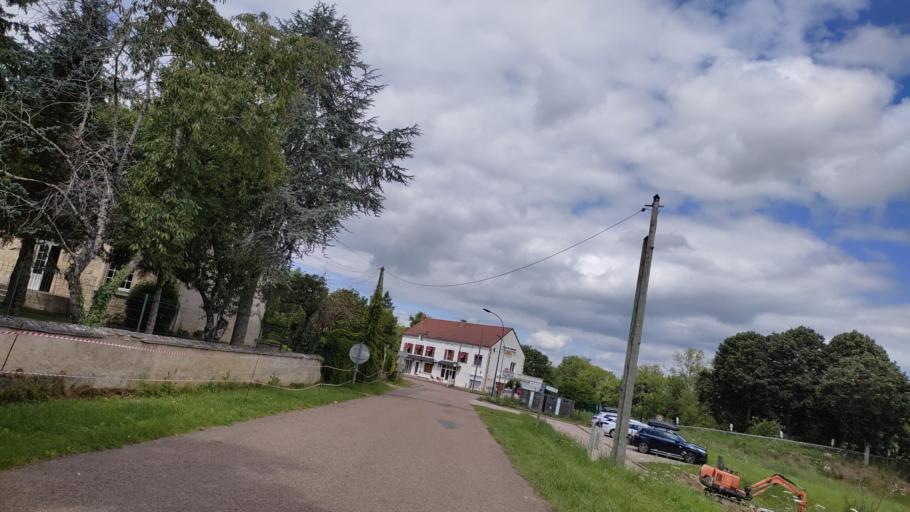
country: FR
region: Bourgogne
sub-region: Departement de la Nievre
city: Corbigny
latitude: 47.3613
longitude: 3.6188
